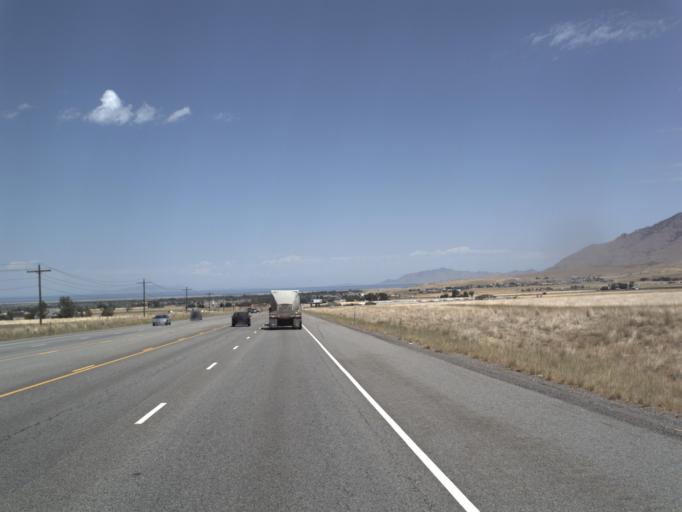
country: US
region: Utah
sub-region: Tooele County
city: Erda
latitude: 40.5804
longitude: -112.2938
